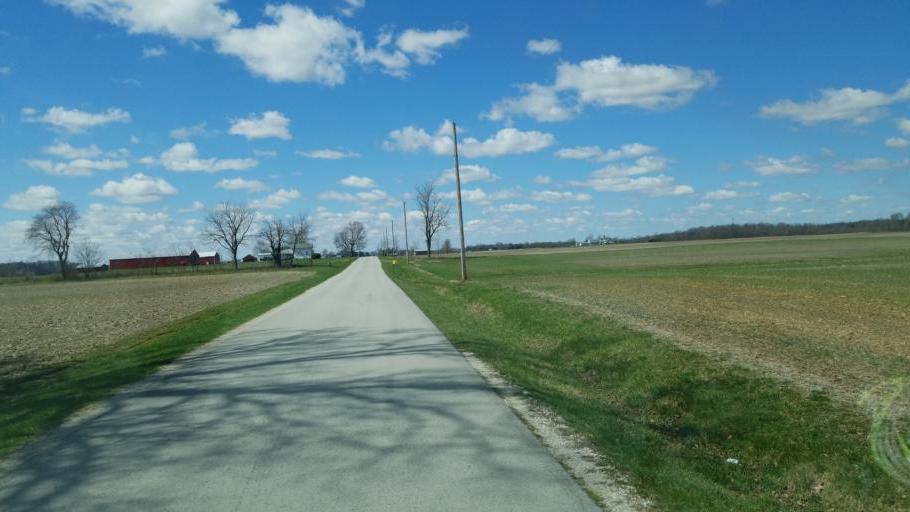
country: US
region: Ohio
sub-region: Seneca County
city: Fostoria
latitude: 41.0938
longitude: -83.5057
